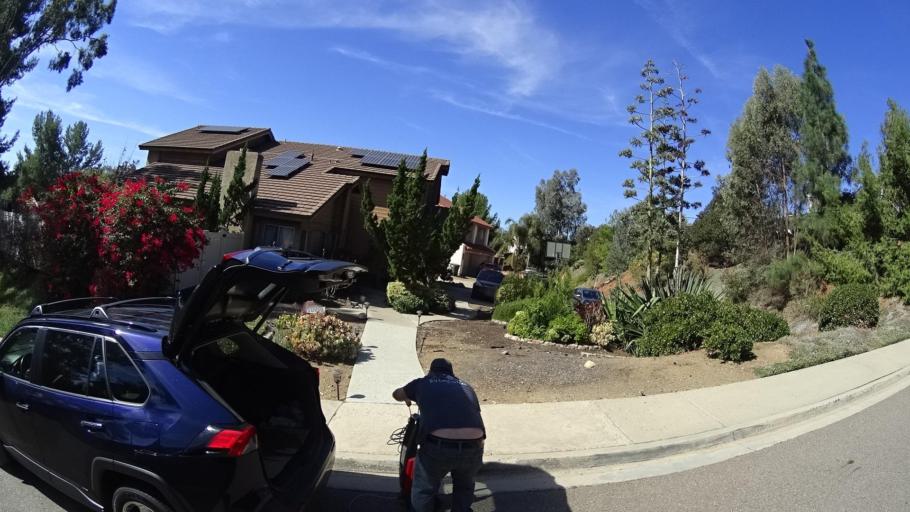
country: US
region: California
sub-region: San Diego County
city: Casa de Oro-Mount Helix
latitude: 32.7519
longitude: -116.9570
